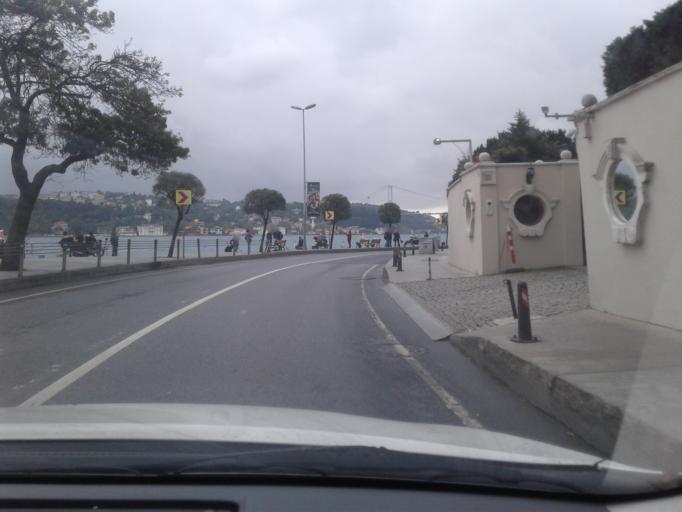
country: TR
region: Istanbul
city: Sisli
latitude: 41.1094
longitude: 29.0590
